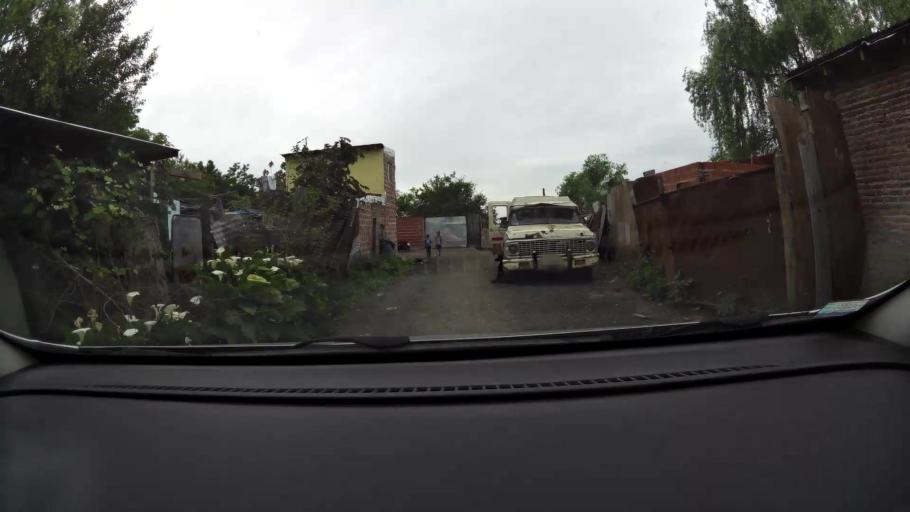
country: AR
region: Buenos Aires
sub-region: Partido de Campana
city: Campana
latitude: -34.1863
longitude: -58.9319
